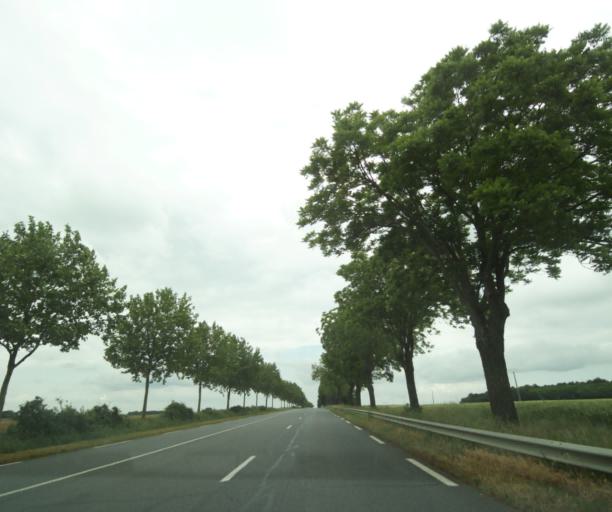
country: FR
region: Poitou-Charentes
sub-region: Departement des Deux-Sevres
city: Saint-Jean-de-Thouars
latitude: 46.9381
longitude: -0.2020
